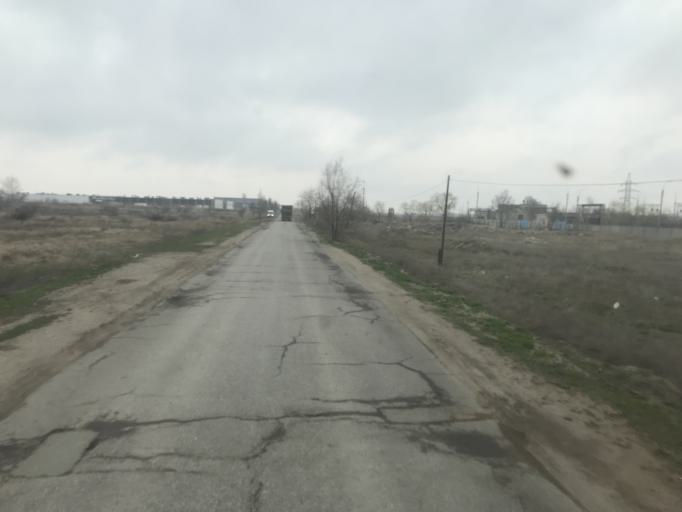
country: RU
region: Volgograd
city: Svetlyy Yar
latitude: 48.5218
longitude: 44.6217
